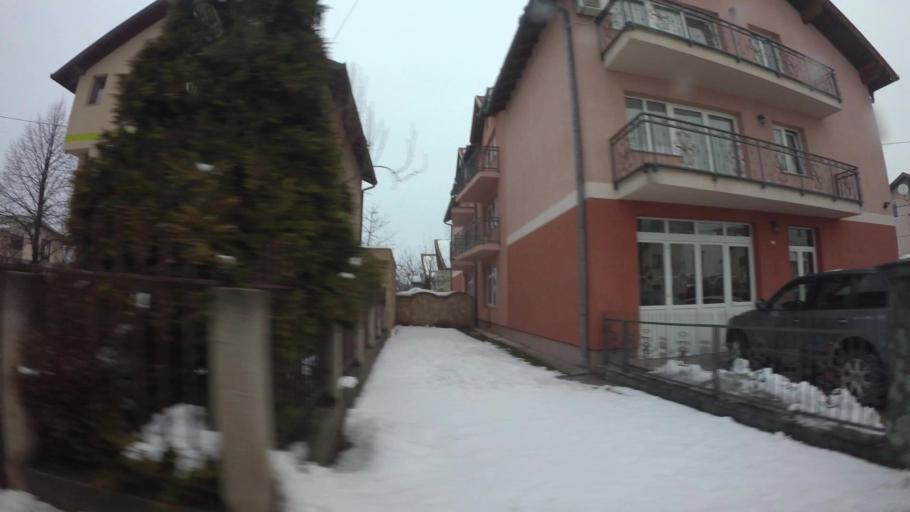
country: BA
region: Federation of Bosnia and Herzegovina
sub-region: Kanton Sarajevo
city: Sarajevo
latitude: 43.8427
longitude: 18.3134
